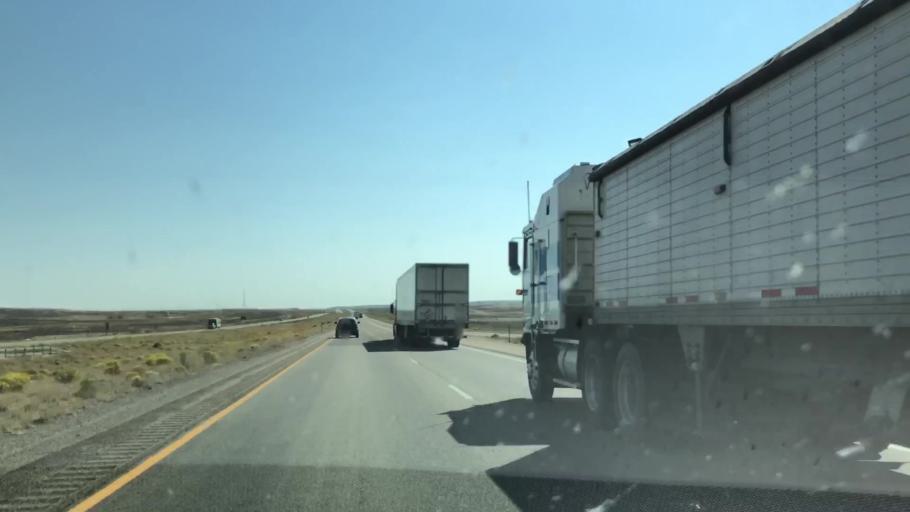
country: US
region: Wyoming
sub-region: Sweetwater County
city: Rock Springs
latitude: 41.6331
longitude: -108.3775
